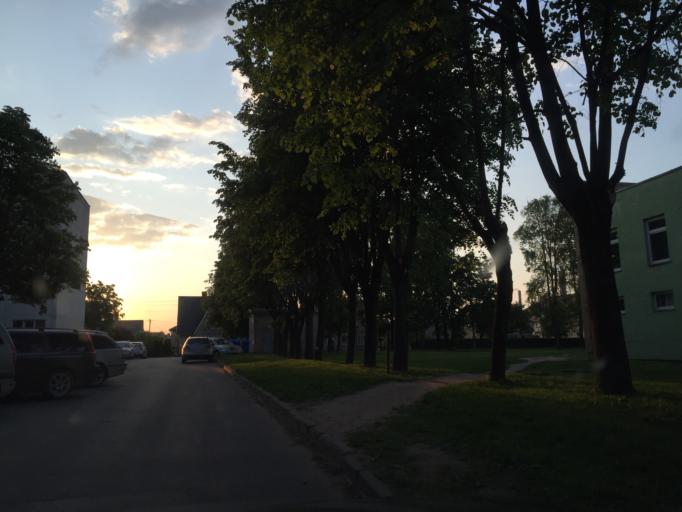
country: LT
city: Kursenai
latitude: 56.0045
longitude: 22.9413
